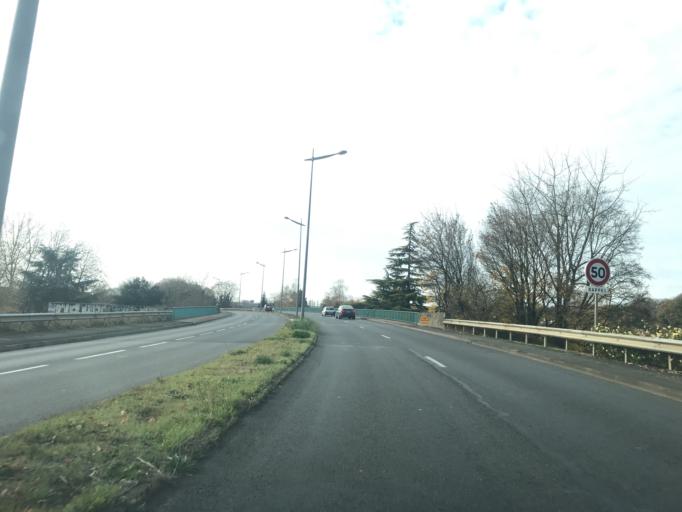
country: FR
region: Poitou-Charentes
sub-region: Departement des Deux-Sevres
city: Niort
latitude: 46.3346
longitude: -0.4773
